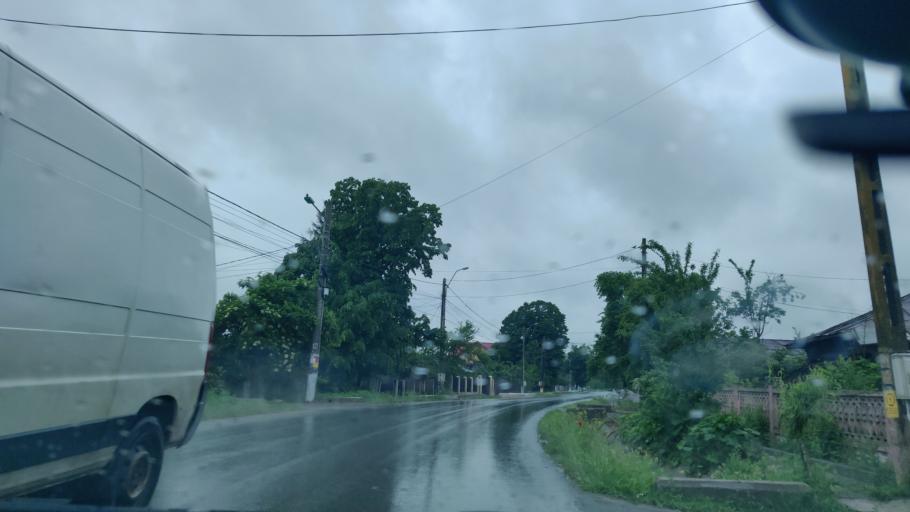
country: RO
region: Giurgiu
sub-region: Comuna Bulbucata
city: Bulbucata
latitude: 44.2742
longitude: 25.8263
